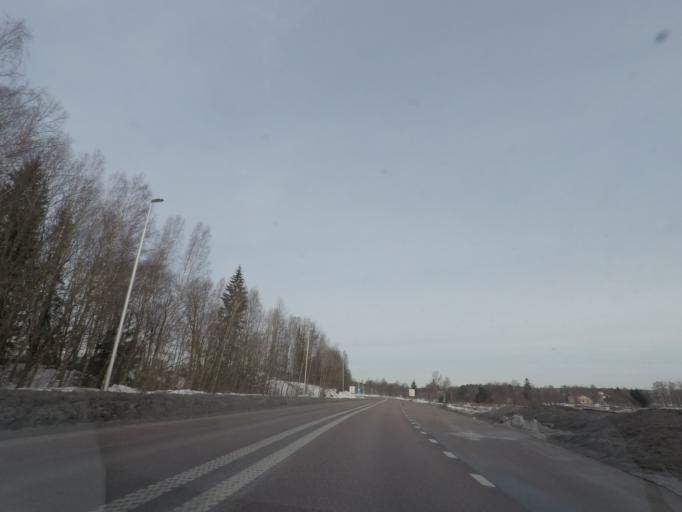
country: SE
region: Vaestmanland
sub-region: Fagersta Kommun
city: Fagersta
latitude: 59.9799
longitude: 15.8167
